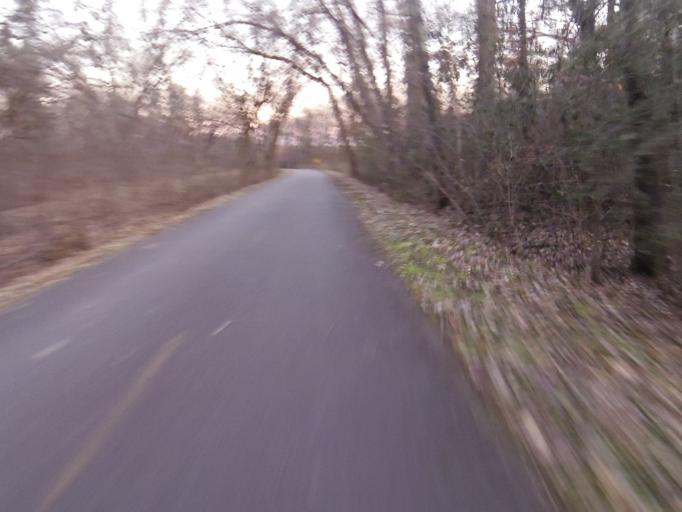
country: US
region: Minnesota
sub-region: Washington County
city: Grant
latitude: 45.1161
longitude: -92.8469
